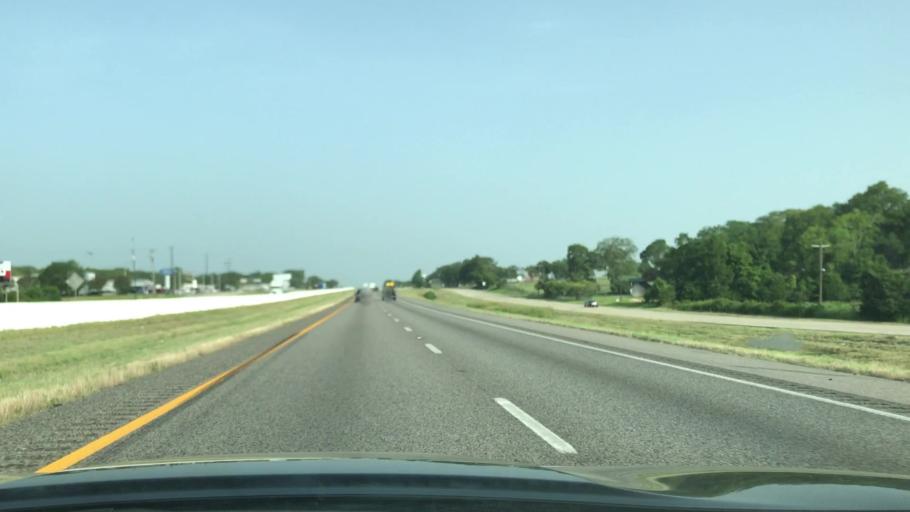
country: US
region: Texas
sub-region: Van Zandt County
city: Canton
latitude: 32.5811
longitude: -95.8612
